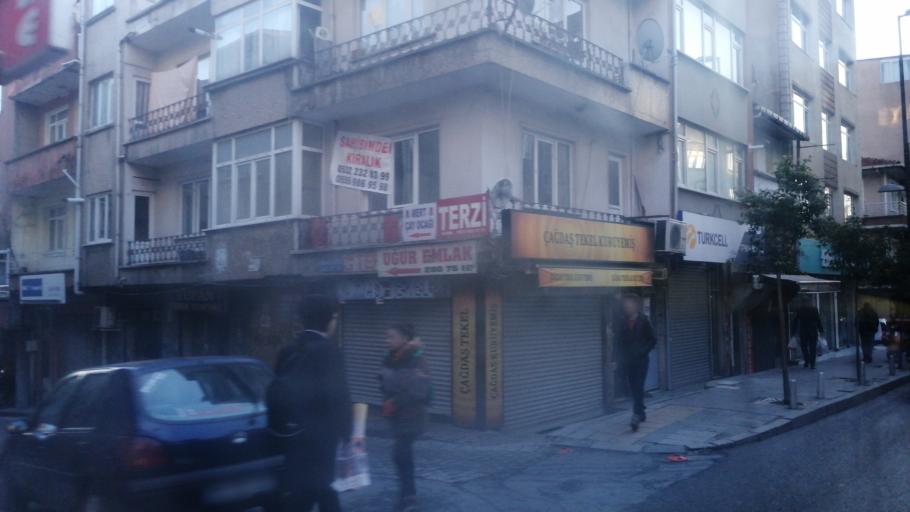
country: TR
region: Istanbul
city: Sisli
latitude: 41.0809
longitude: 28.9931
